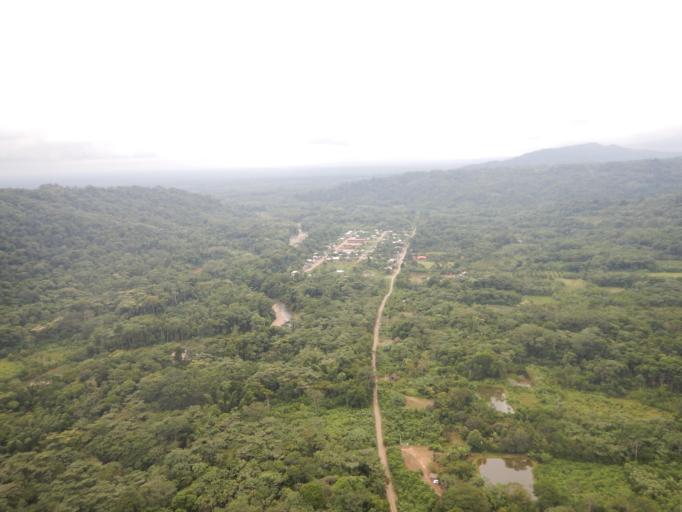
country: BO
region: Cochabamba
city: Chimore
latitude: -17.2559
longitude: -64.6605
